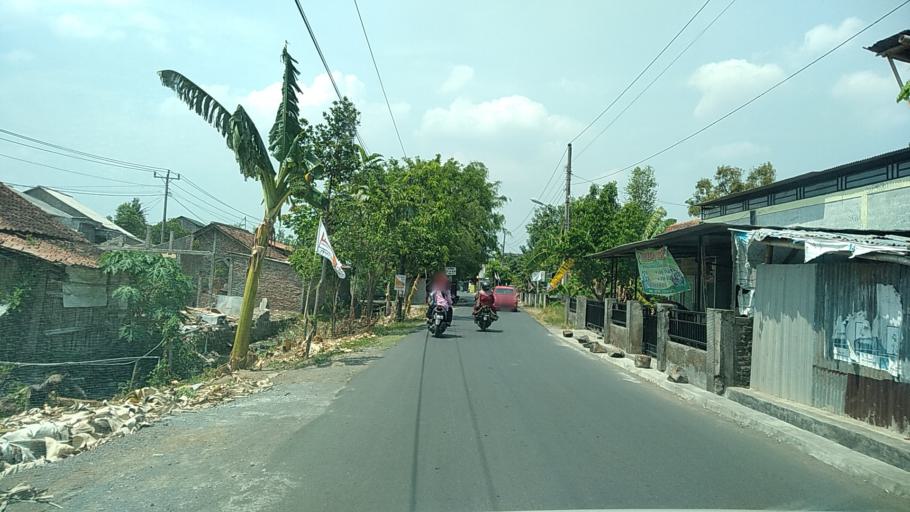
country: ID
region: Central Java
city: Mranggen
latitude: -7.0185
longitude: 110.4827
